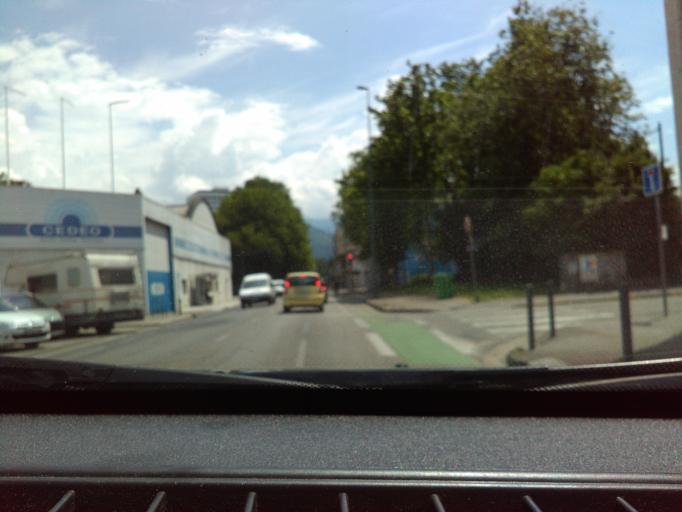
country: FR
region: Rhone-Alpes
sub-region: Departement de l'Isere
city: Grenoble
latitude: 45.1709
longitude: 5.7266
